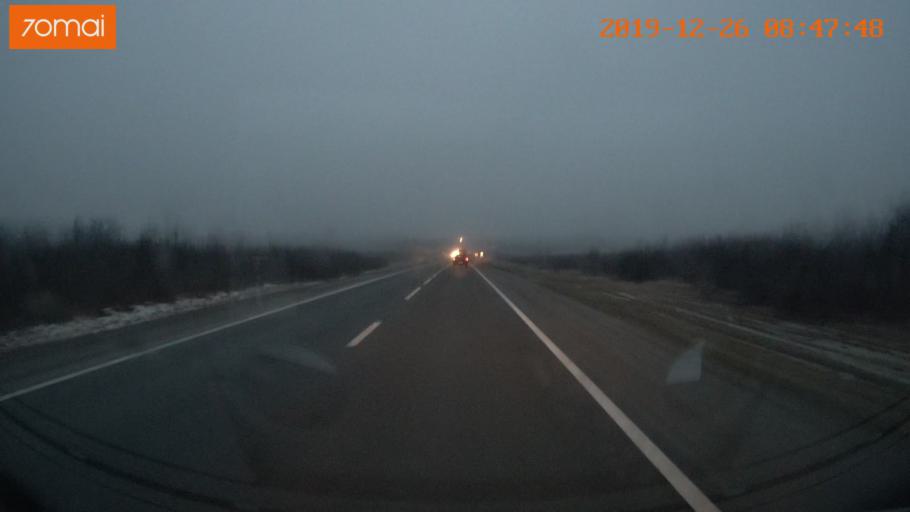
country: RU
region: Jaroslavl
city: Prechistoye
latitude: 58.6276
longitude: 40.3295
